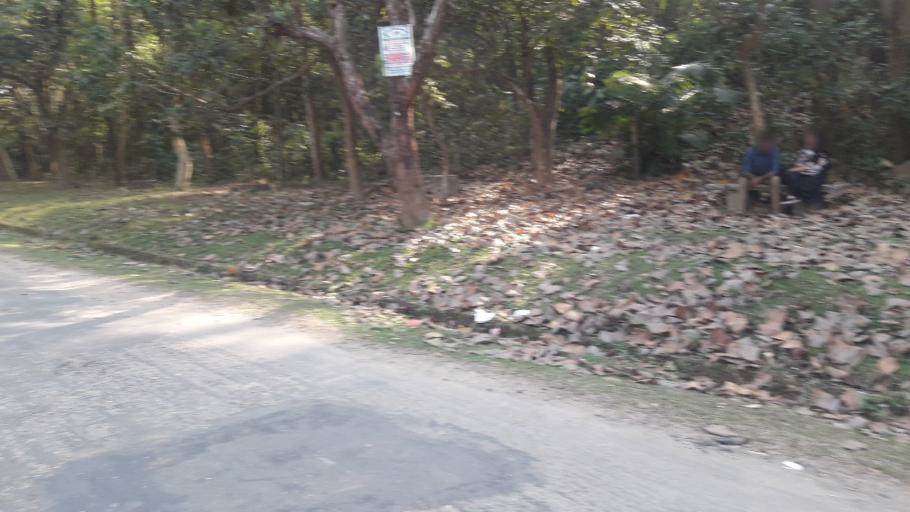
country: BD
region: Chittagong
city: Chittagong
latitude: 22.4676
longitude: 91.7885
